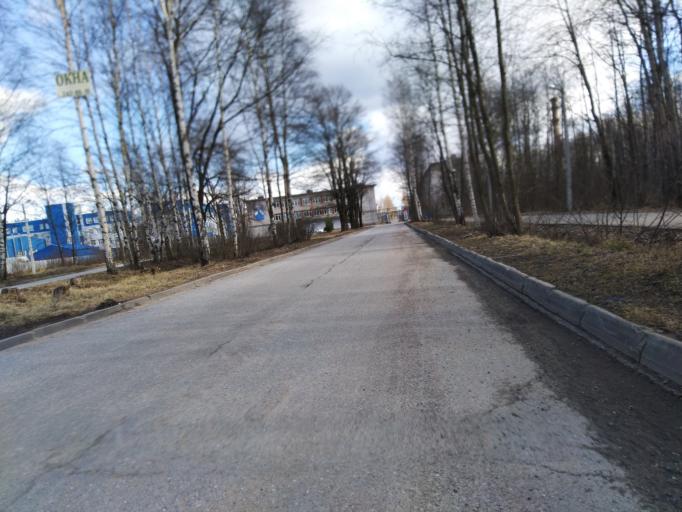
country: RU
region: Leningrad
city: Novoye Devyatkino
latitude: 60.0963
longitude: 30.4757
